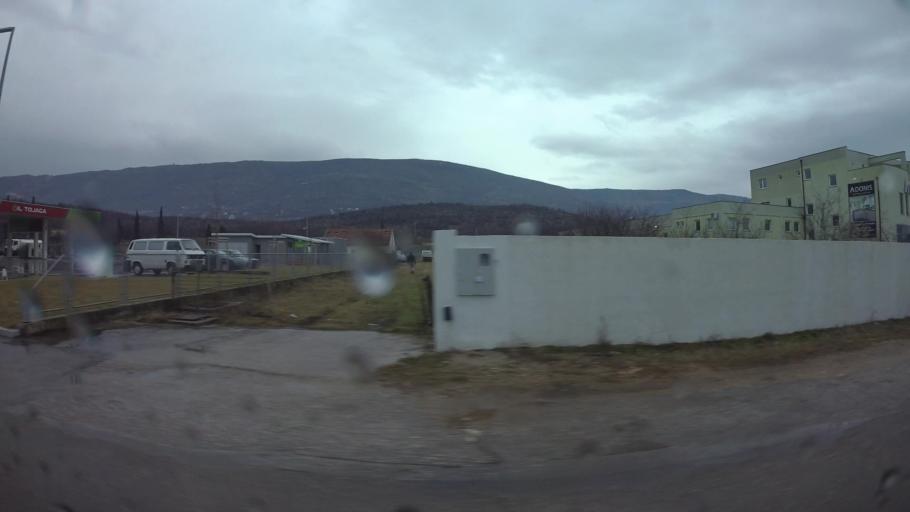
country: BA
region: Federation of Bosnia and Herzegovina
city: Rodoc
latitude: 43.2902
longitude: 17.8471
